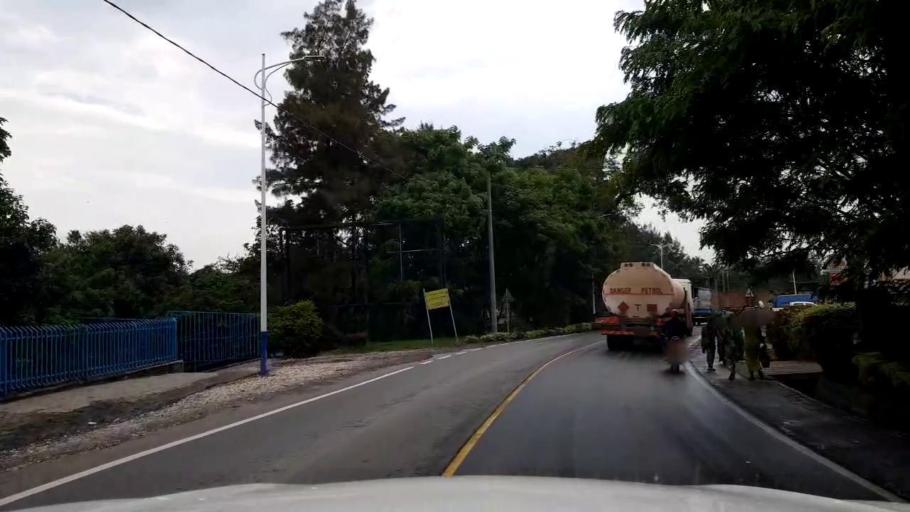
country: RW
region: Western Province
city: Gisenyi
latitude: -1.7031
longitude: 29.2621
